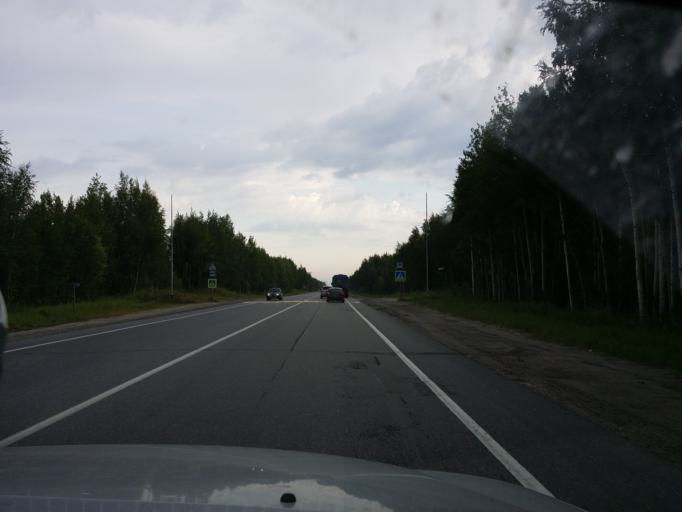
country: RU
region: Khanty-Mansiyskiy Avtonomnyy Okrug
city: Megion
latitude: 61.0627
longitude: 76.1149
